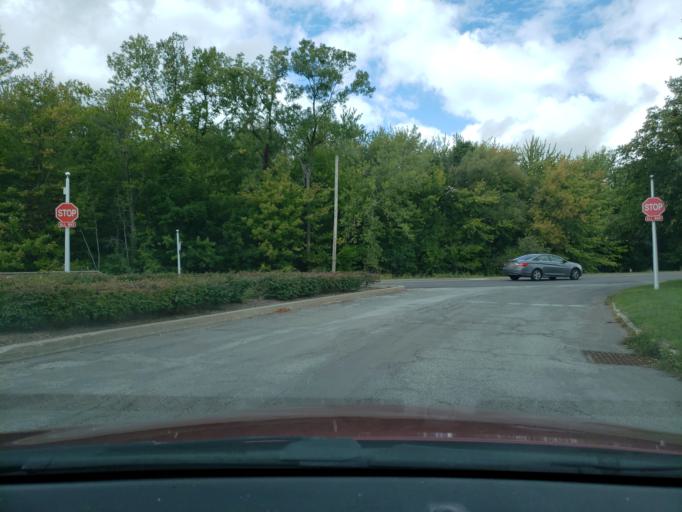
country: US
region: New York
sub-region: Monroe County
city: North Gates
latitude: 43.1481
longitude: -77.7403
